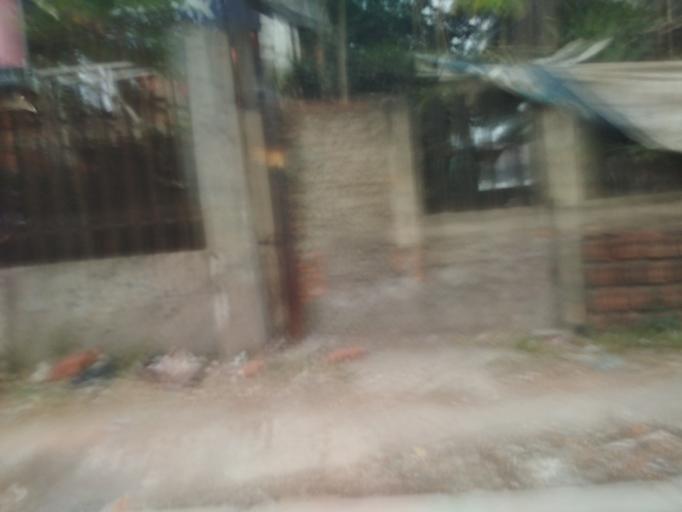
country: ID
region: West Java
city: Caringin
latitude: -6.7080
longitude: 106.8223
